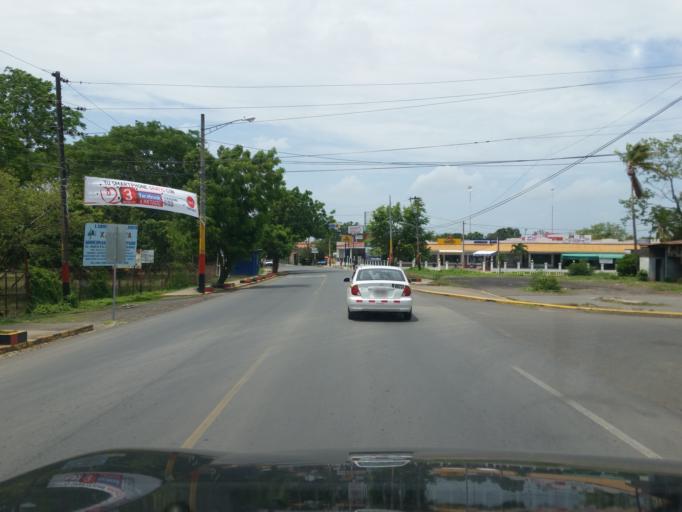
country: NI
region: Granada
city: Nandaime
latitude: 11.7575
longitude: -86.0461
